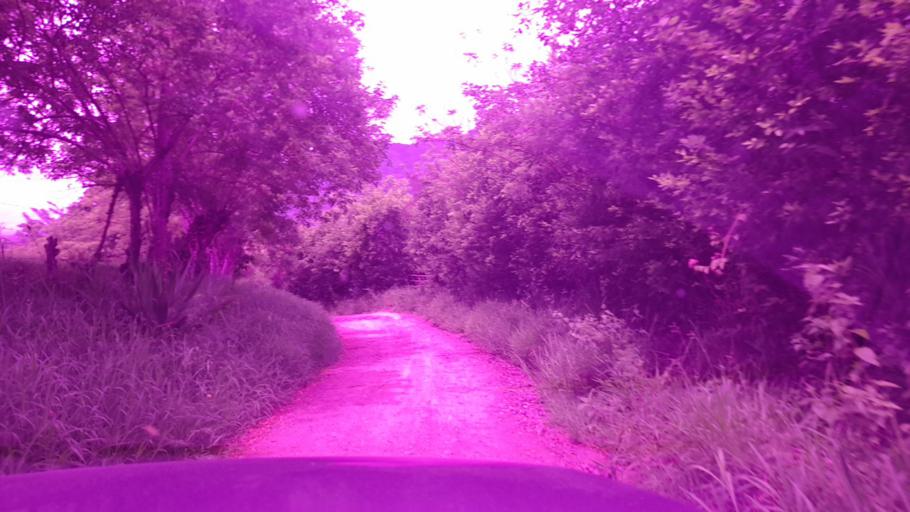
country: CO
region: Valle del Cauca
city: Andalucia
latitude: 4.1656
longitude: -76.0913
